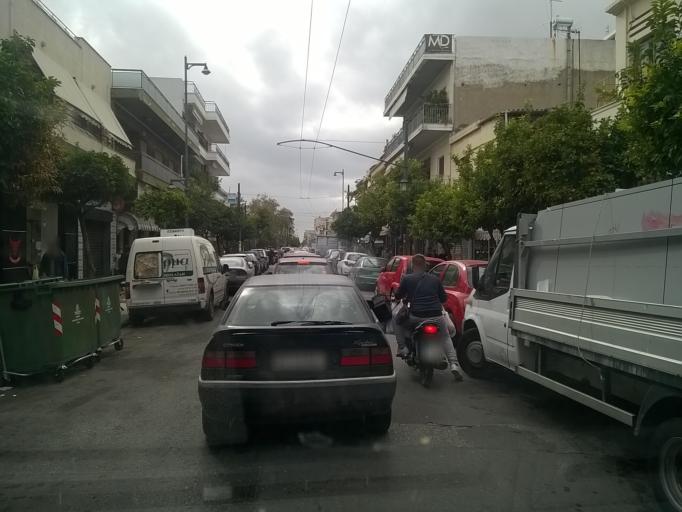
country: GR
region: Attica
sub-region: Nomarchia Athinas
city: Moskhaton
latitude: 37.9532
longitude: 23.6794
